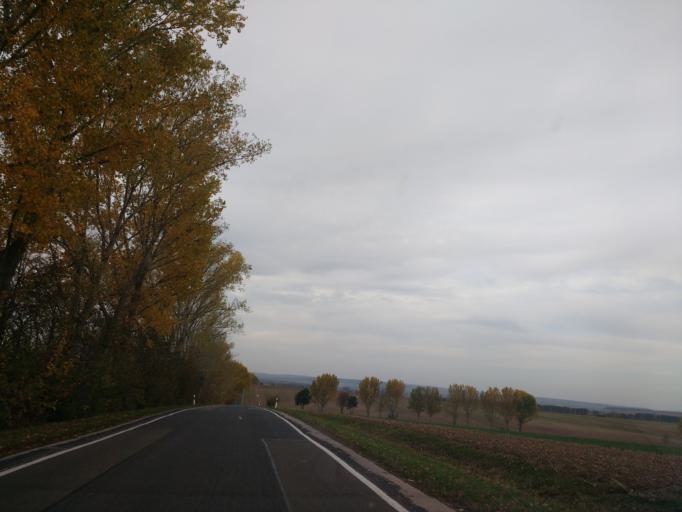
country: DE
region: Thuringia
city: Heroldishausen
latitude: 51.1460
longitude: 10.5220
